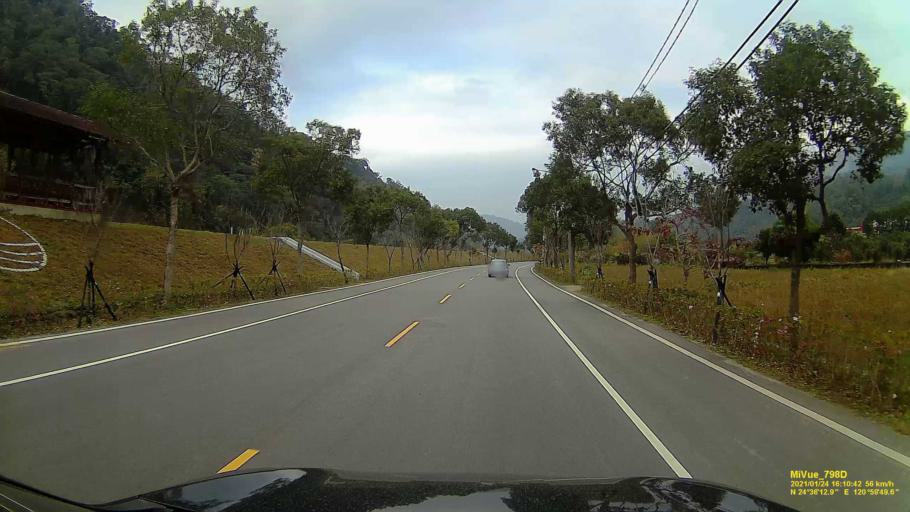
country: TW
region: Taiwan
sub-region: Miaoli
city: Miaoli
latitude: 24.6037
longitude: 120.9972
